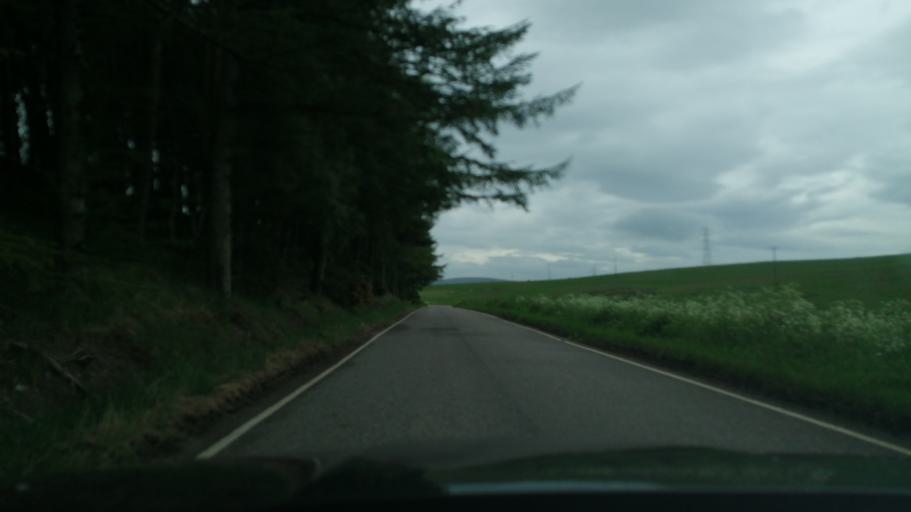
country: GB
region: Scotland
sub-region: Moray
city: Cullen
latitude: 57.5970
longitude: -2.8555
